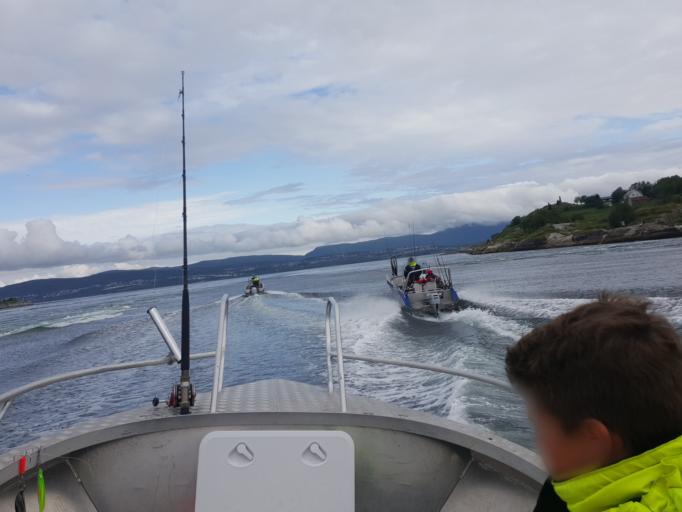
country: NO
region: Nordland
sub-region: Bodo
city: Loding
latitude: 67.2308
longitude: 14.6138
